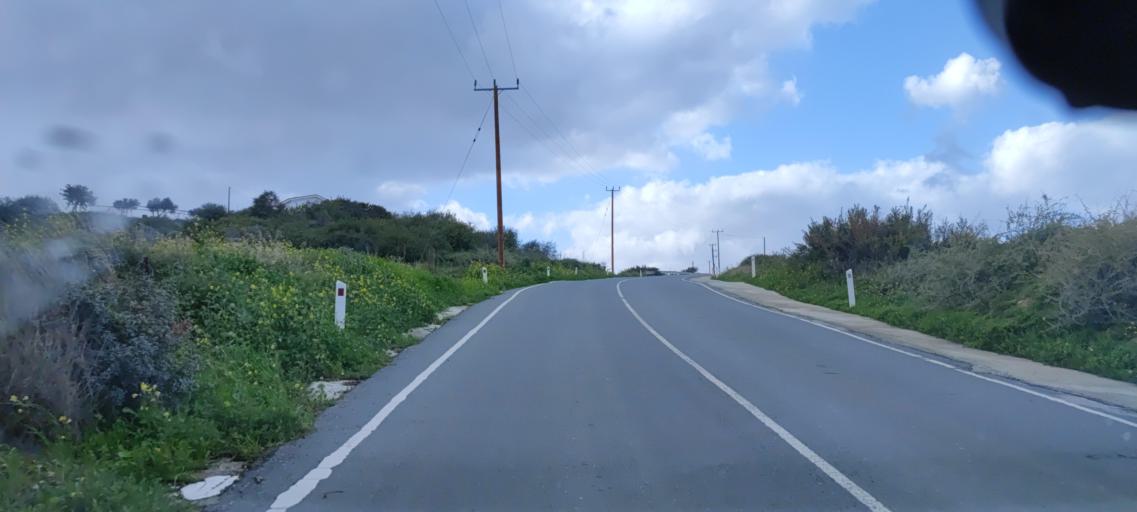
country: CY
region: Limassol
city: Pissouri
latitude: 34.6652
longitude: 32.7121
